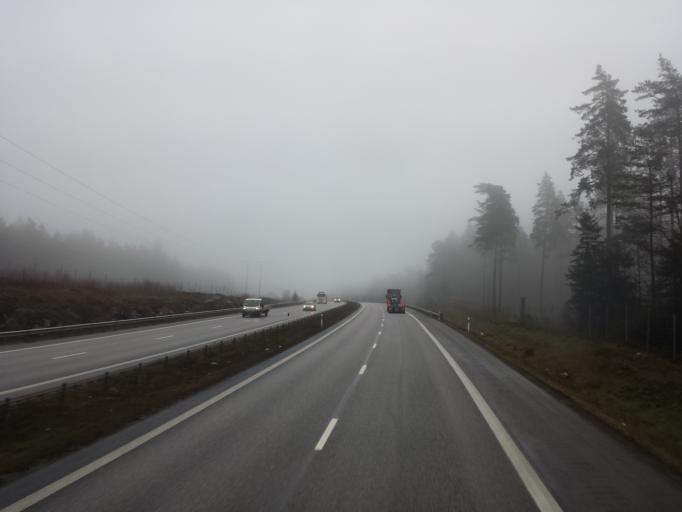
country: SE
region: OEstergoetland
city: Lindo
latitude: 58.6780
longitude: 16.3007
